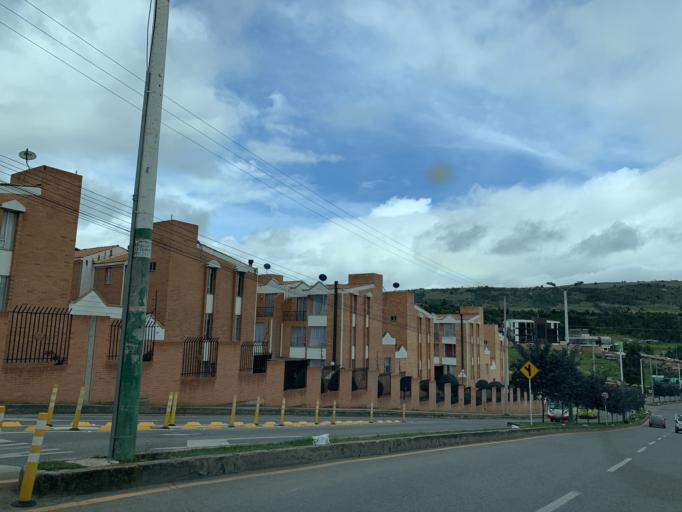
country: CO
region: Boyaca
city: Tunja
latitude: 5.5716
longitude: -73.3340
